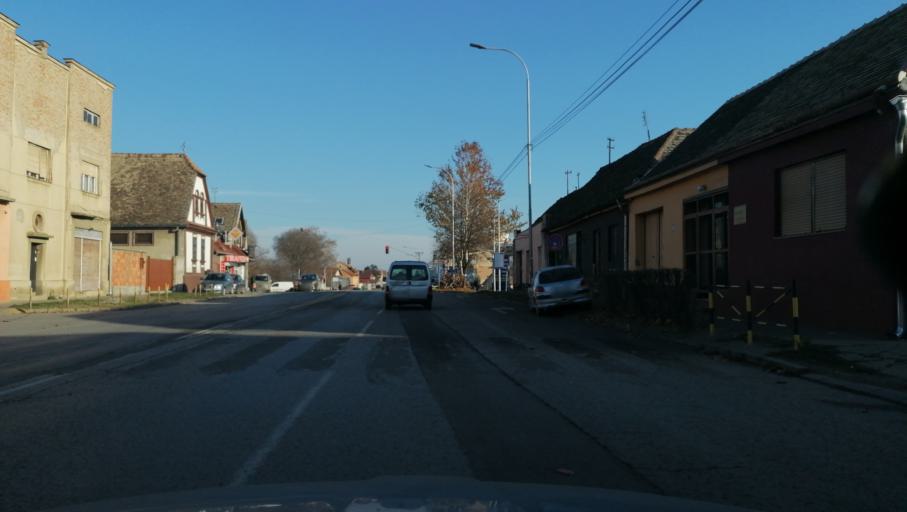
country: RS
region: Autonomna Pokrajina Vojvodina
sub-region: Sremski Okrug
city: Sremska Mitrovica
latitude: 44.9716
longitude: 19.6183
